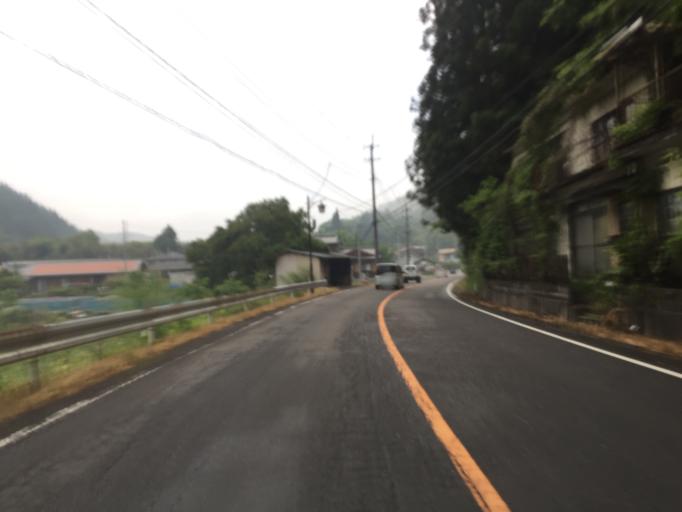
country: JP
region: Fukushima
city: Ishikawa
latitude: 37.1644
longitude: 140.4685
